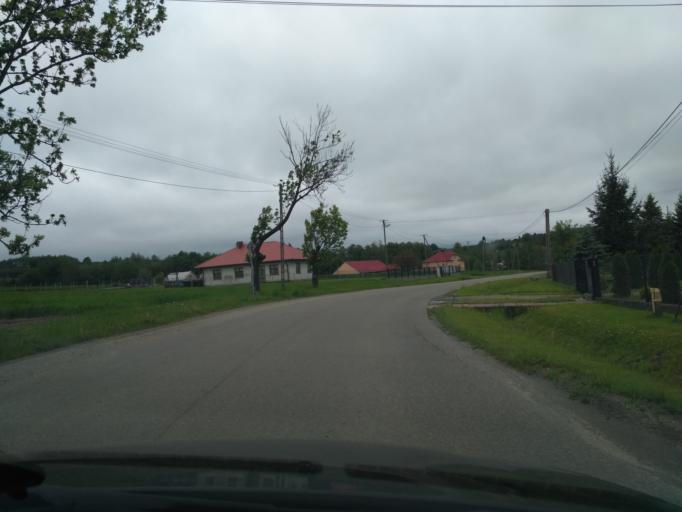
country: PL
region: Subcarpathian Voivodeship
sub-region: Powiat jasielski
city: Brzyska
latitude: 49.8407
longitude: 21.3875
